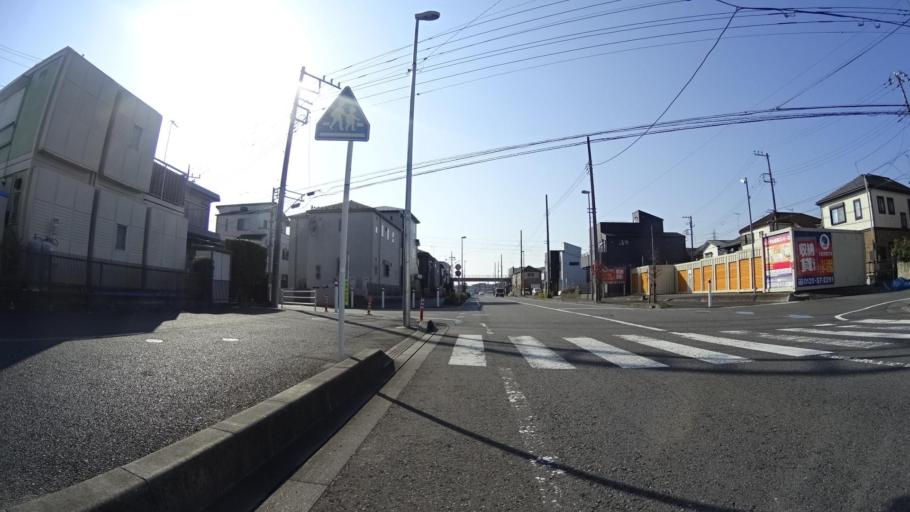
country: JP
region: Tokyo
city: Hachioji
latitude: 35.5937
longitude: 139.3279
